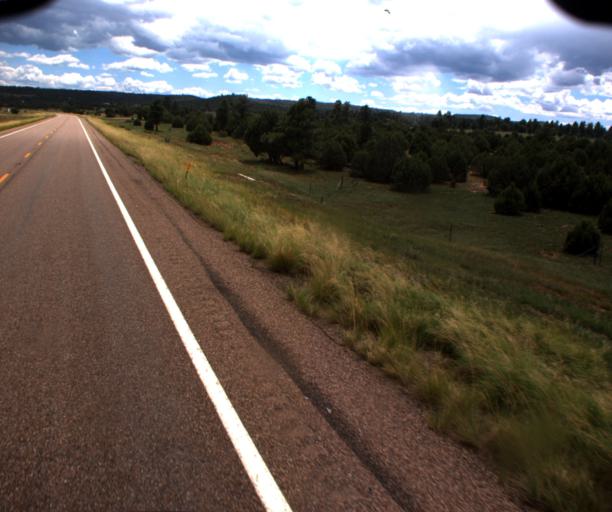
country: US
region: Arizona
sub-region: Navajo County
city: Linden
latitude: 34.3539
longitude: -110.3148
